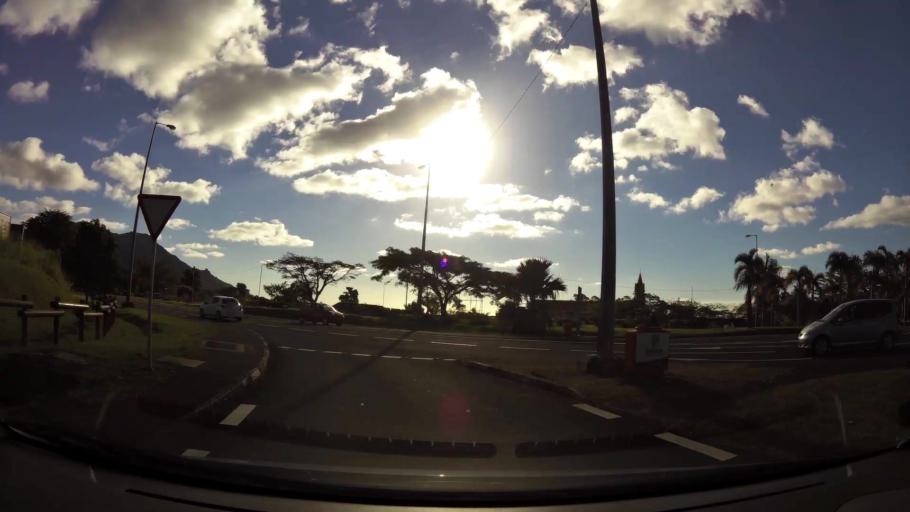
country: MU
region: Plaines Wilhems
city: Quatre Bornes
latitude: -20.2576
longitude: 57.4878
